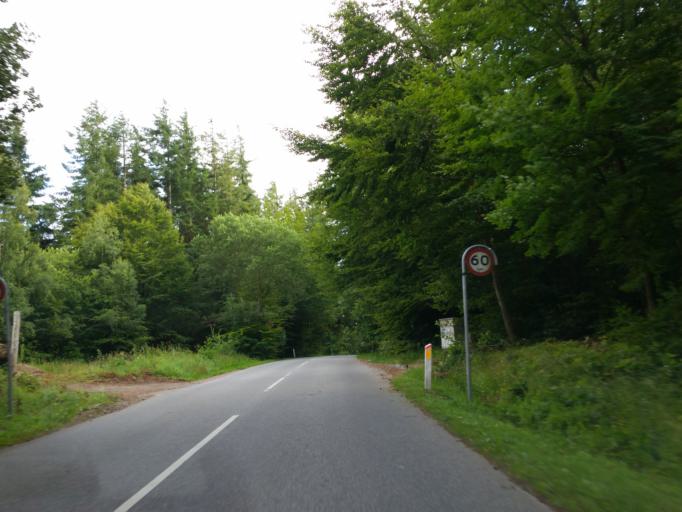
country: DK
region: South Denmark
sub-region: Vejle Kommune
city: Borkop
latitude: 55.6875
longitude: 9.6181
